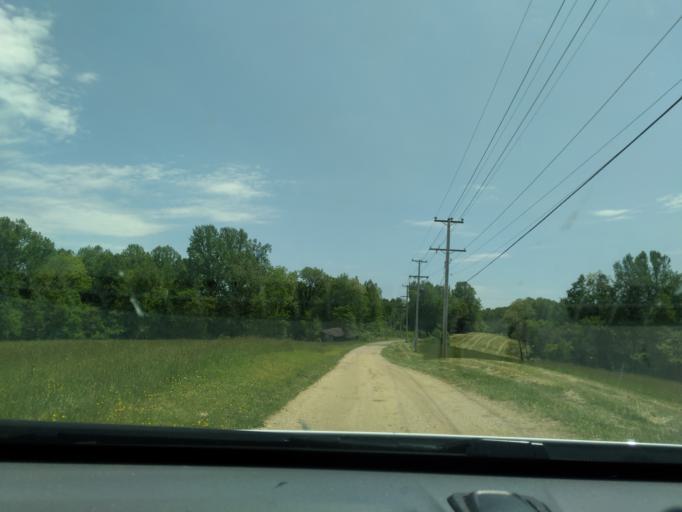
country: US
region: Maryland
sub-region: Prince George's County
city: Marlboro Meadows
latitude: 38.8522
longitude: -76.7092
